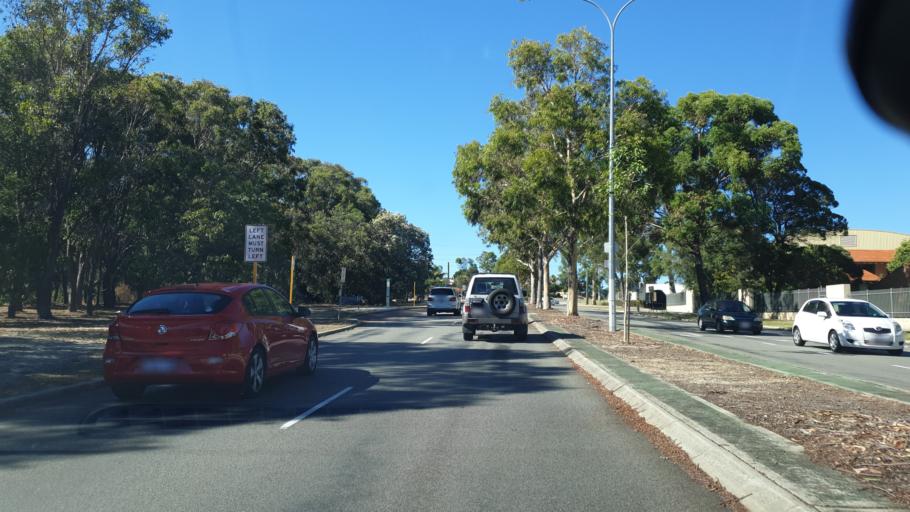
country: AU
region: Western Australia
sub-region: Canning
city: Rossmoyne
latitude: -32.0476
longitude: 115.8599
